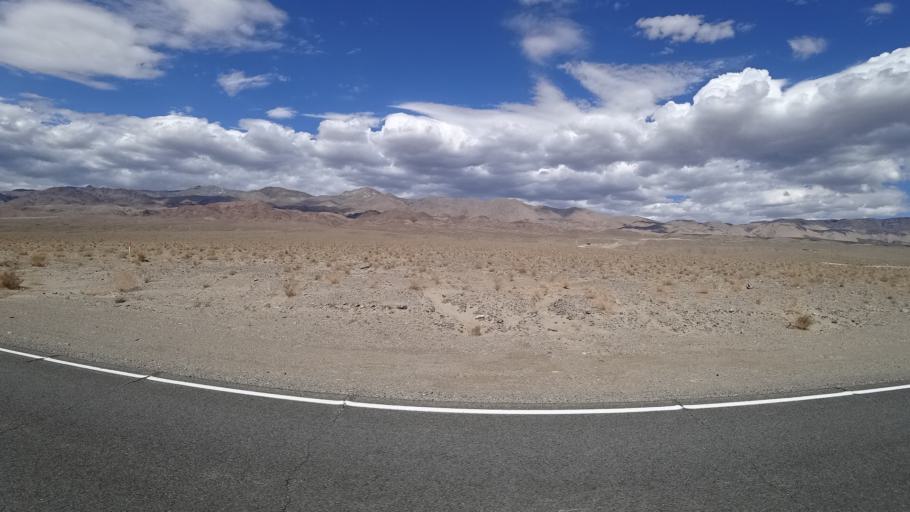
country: US
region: California
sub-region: Inyo County
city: Lone Pine
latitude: 36.4751
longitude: -117.8563
